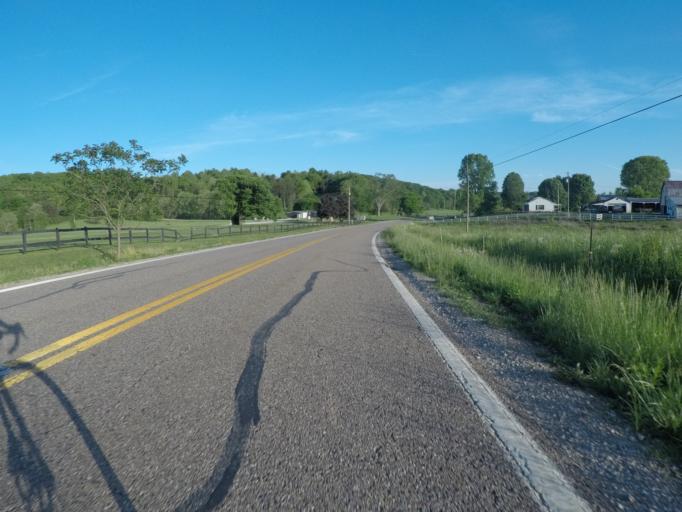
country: US
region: West Virginia
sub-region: Cabell County
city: Huntington
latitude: 38.5426
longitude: -82.4614
